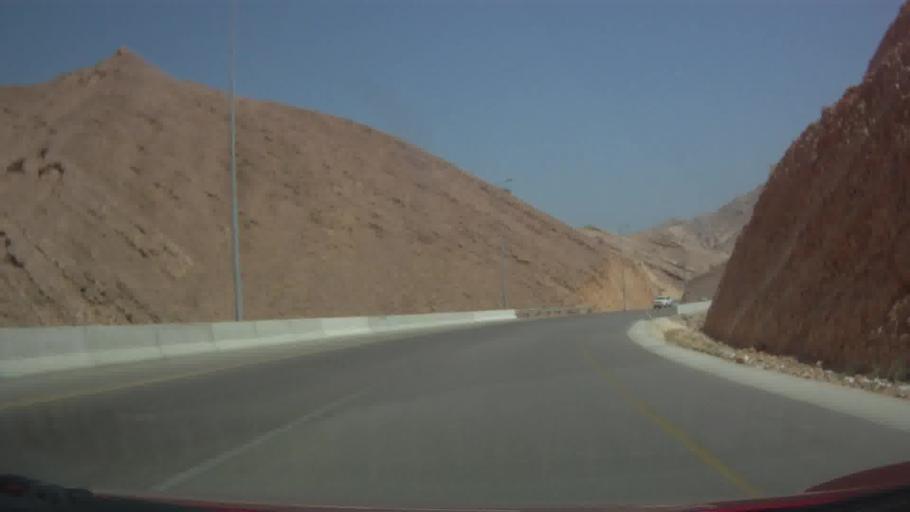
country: OM
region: Muhafazat Masqat
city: Muscat
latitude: 23.5409
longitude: 58.6386
